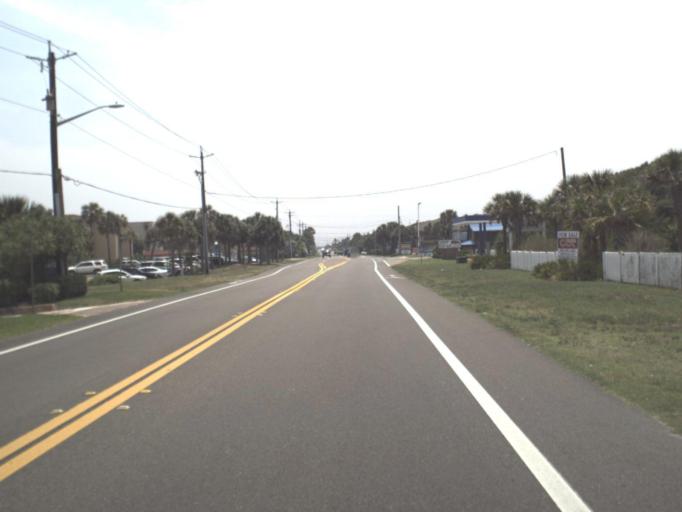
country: US
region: Florida
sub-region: Nassau County
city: Fernandina Beach
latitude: 30.6209
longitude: -81.4409
